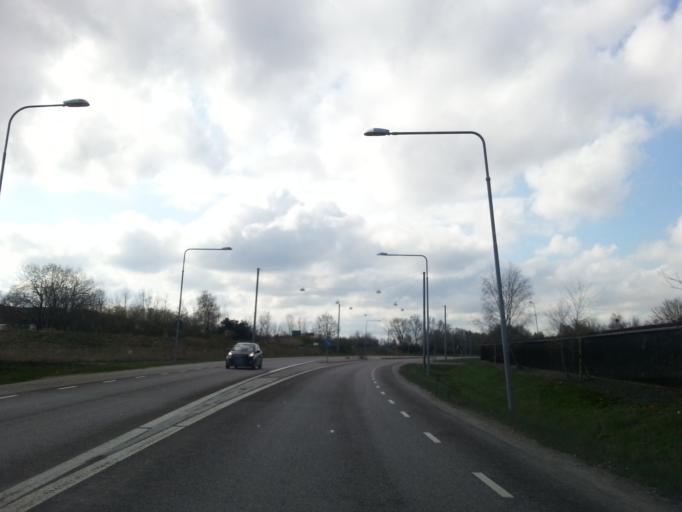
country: SE
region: Vaestra Goetaland
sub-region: Goteborg
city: Gardsten
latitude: 57.7941
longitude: 12.0023
